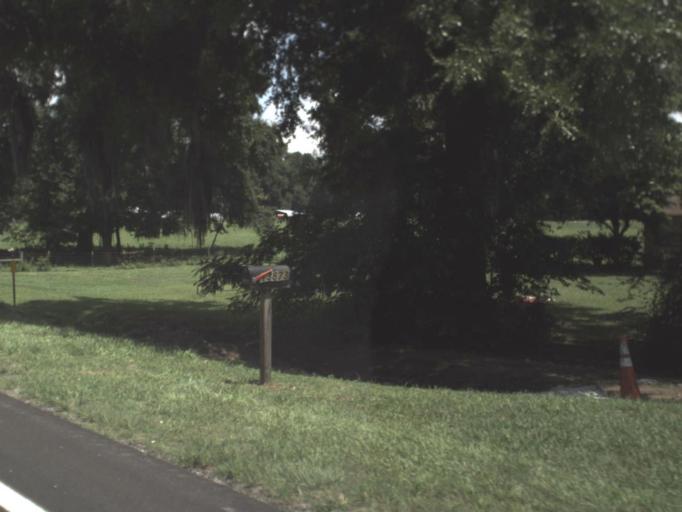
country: US
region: Florida
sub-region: Alachua County
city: Alachua
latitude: 29.7824
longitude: -82.4582
